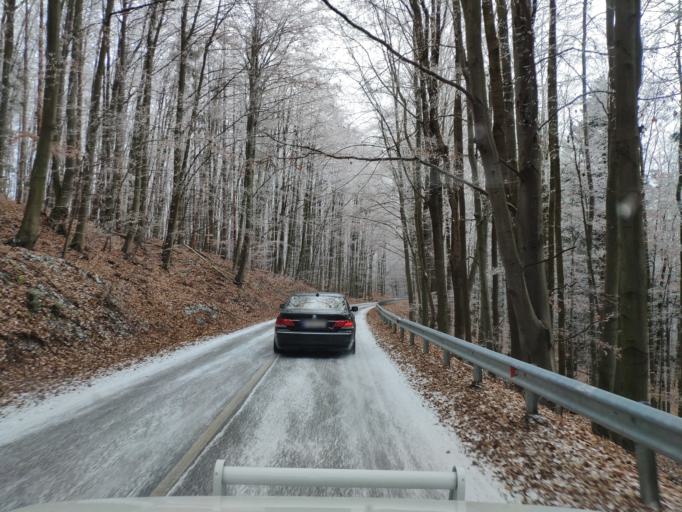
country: SK
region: Kosicky
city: Dobsina
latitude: 48.7981
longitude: 20.4813
